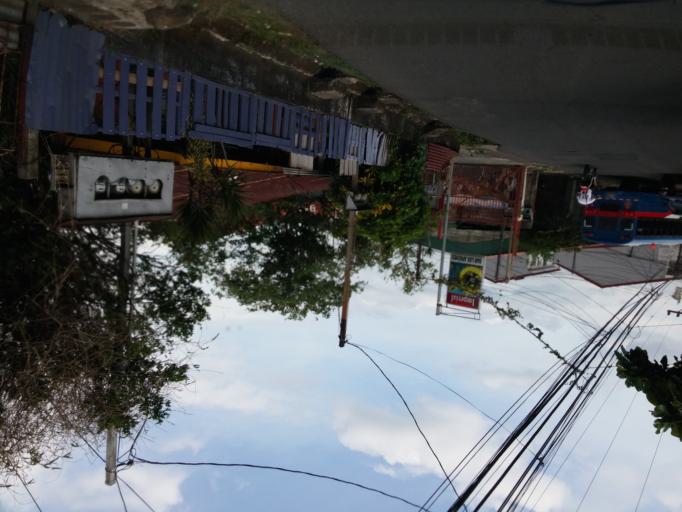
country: CR
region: Alajuela
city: Alajuela
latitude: 10.0050
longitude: -84.2033
